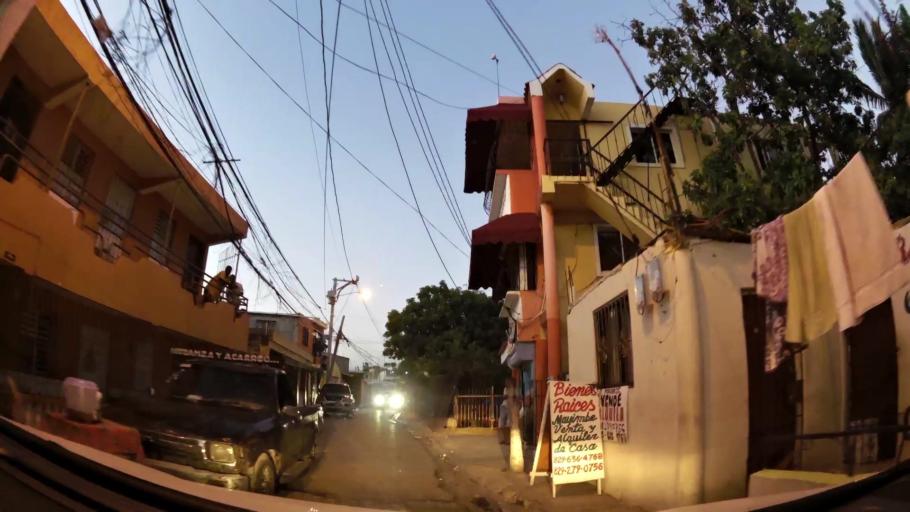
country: DO
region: Santo Domingo
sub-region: Santo Domingo
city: Santo Domingo Este
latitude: 18.4990
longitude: -69.8372
